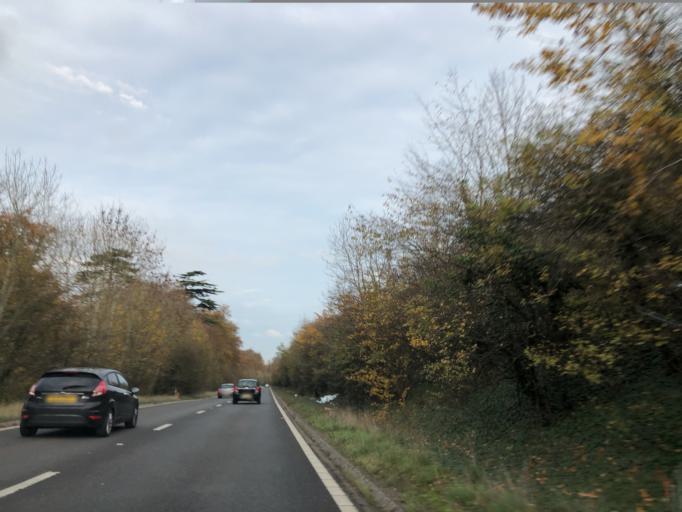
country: GB
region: England
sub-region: Royal Borough of Windsor and Maidenhead
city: Bisham
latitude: 51.5464
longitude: -0.7837
